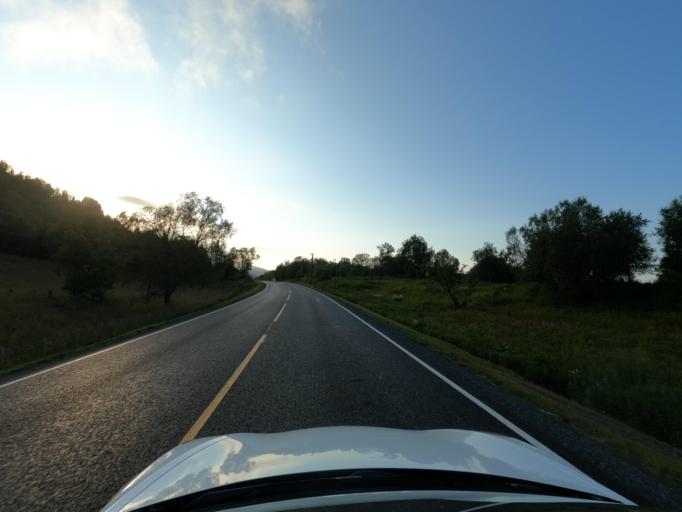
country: NO
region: Troms
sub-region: Skanland
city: Evenskjer
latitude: 68.6742
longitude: 16.5676
